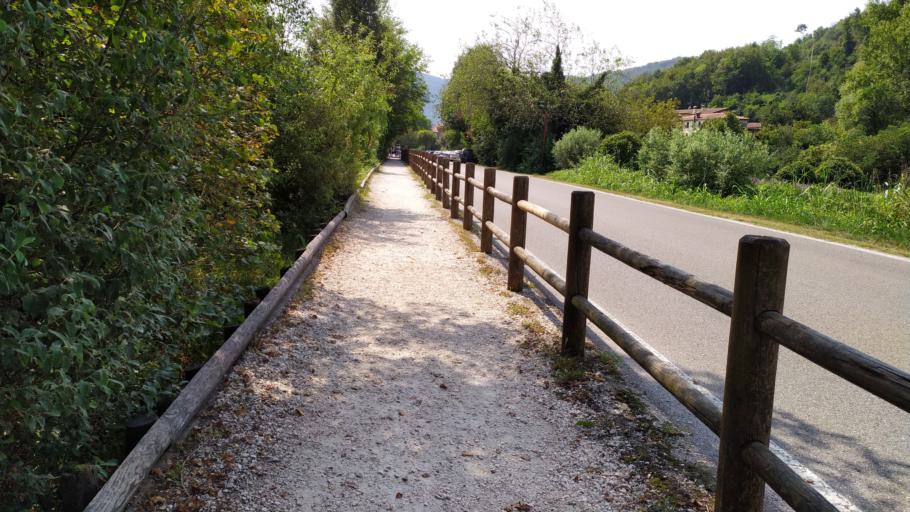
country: IT
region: Veneto
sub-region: Provincia di Vicenza
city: Arcugnano-Torri
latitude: 45.4760
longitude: 11.5418
